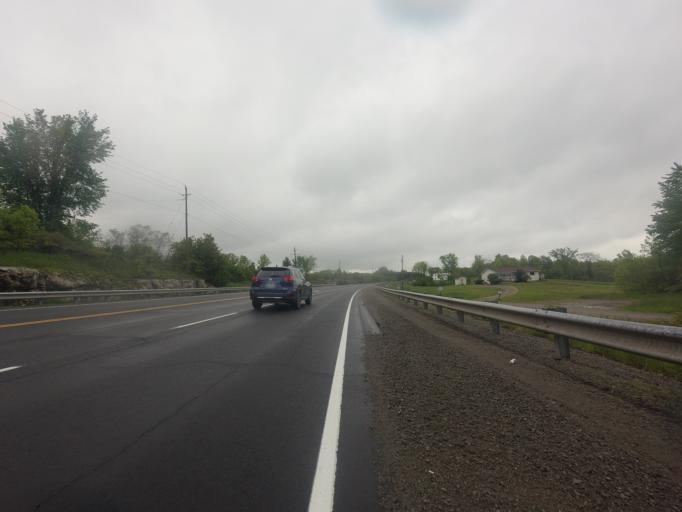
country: CA
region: Ontario
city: Perth
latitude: 44.7148
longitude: -76.1743
